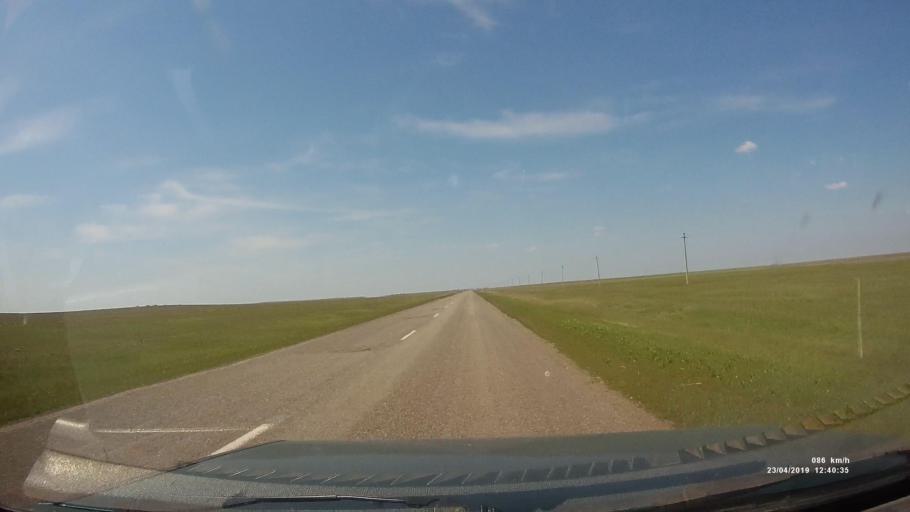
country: RU
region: Kalmykiya
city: Yashalta
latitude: 46.4414
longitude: 42.6943
